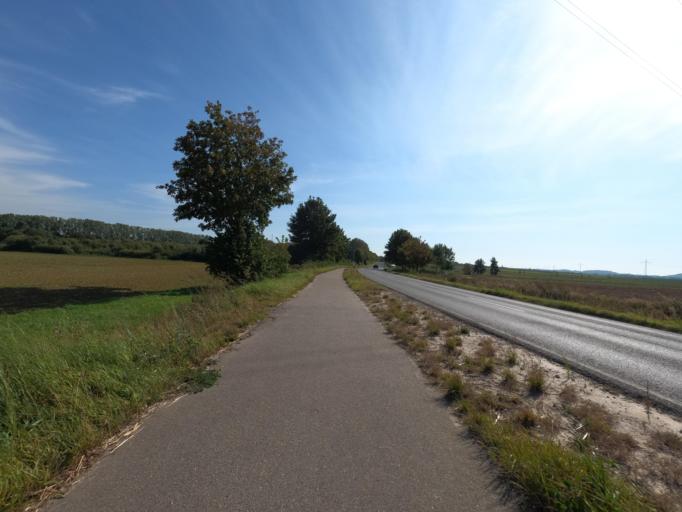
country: DE
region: North Rhine-Westphalia
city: Siersdorf
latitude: 50.9095
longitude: 6.2177
